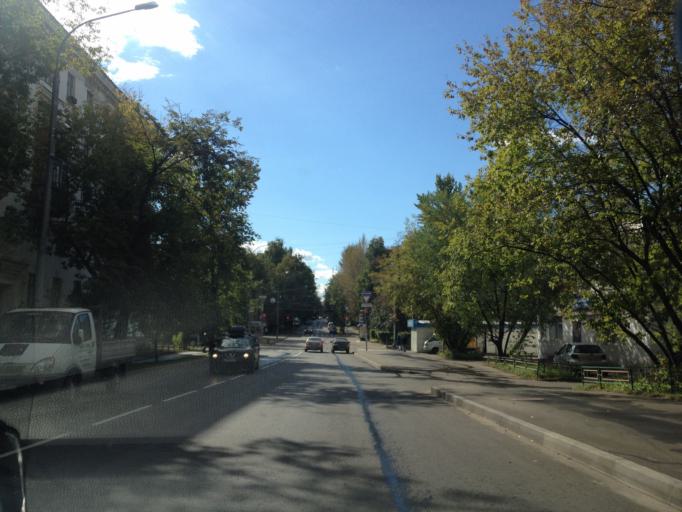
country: RU
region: Moscow
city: Metrogorodok
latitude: 55.7979
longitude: 37.7938
